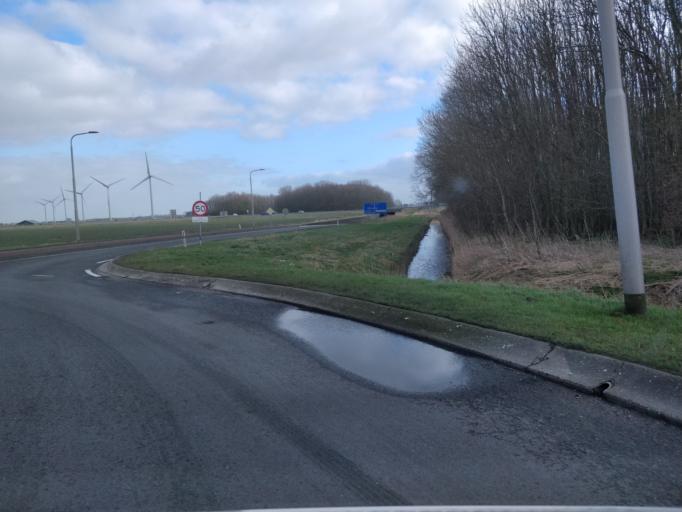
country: NL
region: Friesland
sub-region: Gemeente Harlingen
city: Harlingen
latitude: 53.1840
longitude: 5.4546
